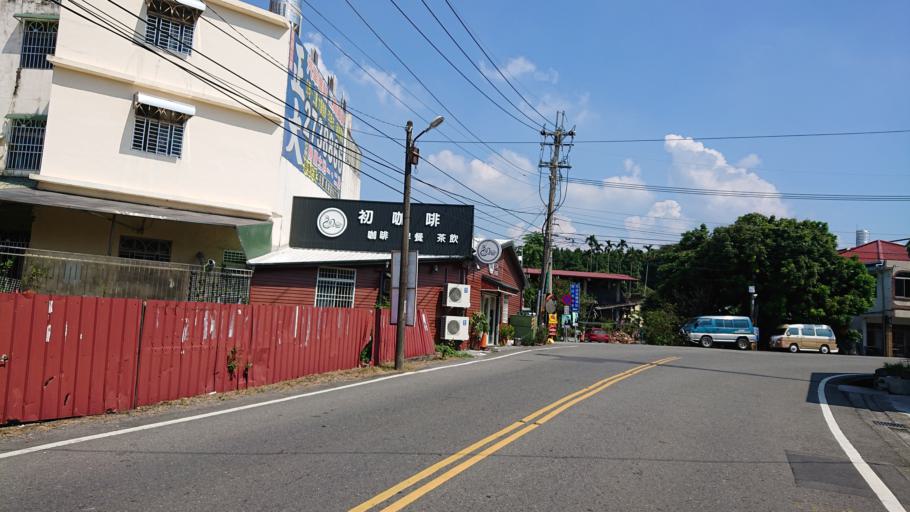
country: TW
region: Taiwan
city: Lugu
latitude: 23.8153
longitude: 120.7237
